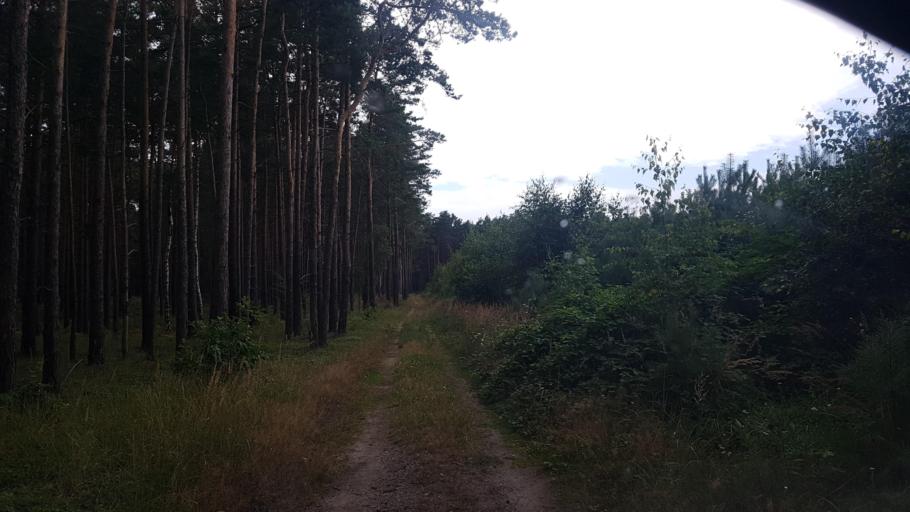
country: DE
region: Brandenburg
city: Sallgast
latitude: 51.5828
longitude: 13.9065
